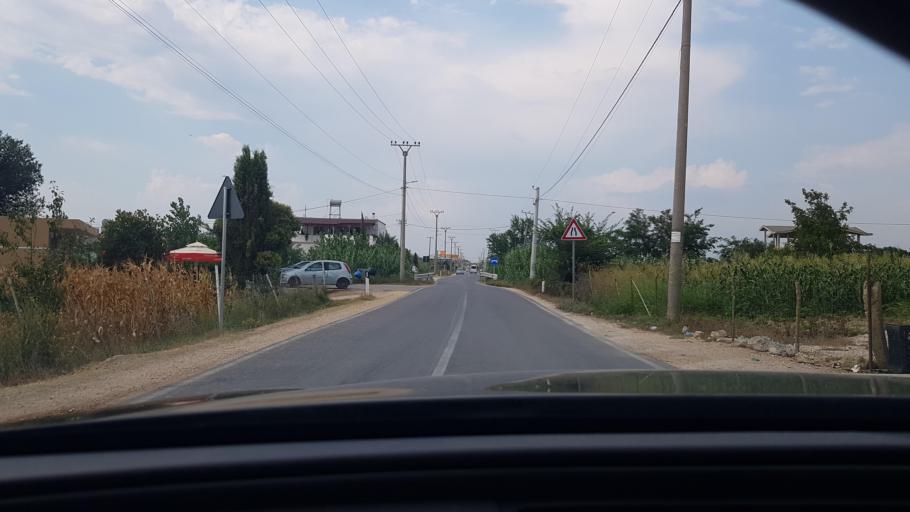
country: AL
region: Durres
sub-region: Rrethi i Durresit
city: Katundi i Ri
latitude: 41.4212
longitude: 19.5488
